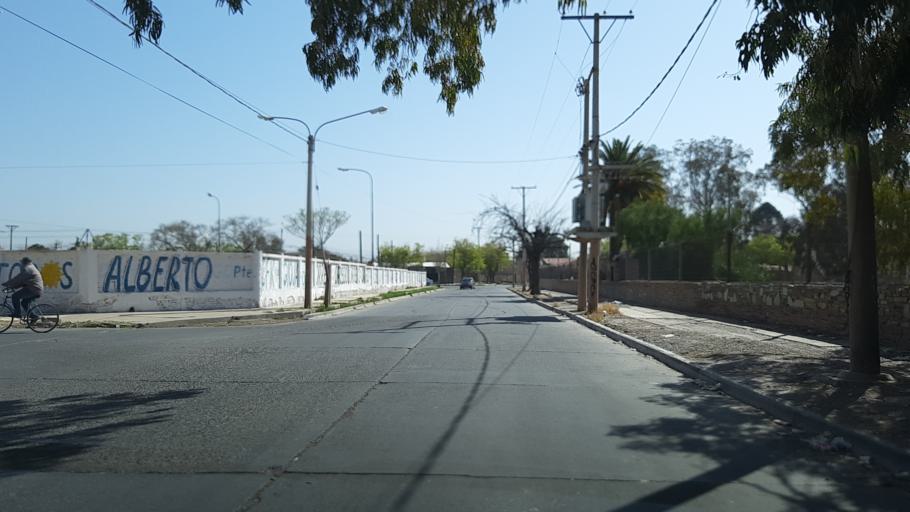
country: AR
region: San Juan
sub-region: Departamento de Santa Lucia
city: Santa Lucia
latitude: -31.5292
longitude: -68.5119
